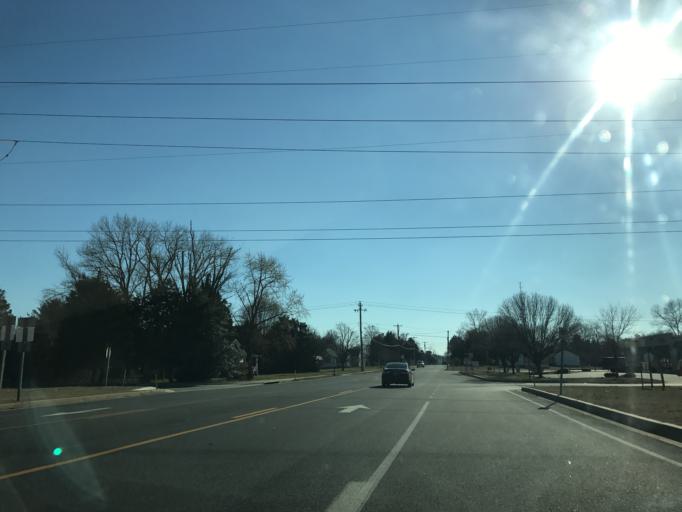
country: US
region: Maryland
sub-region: Caroline County
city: Denton
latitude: 38.8941
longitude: -75.8199
